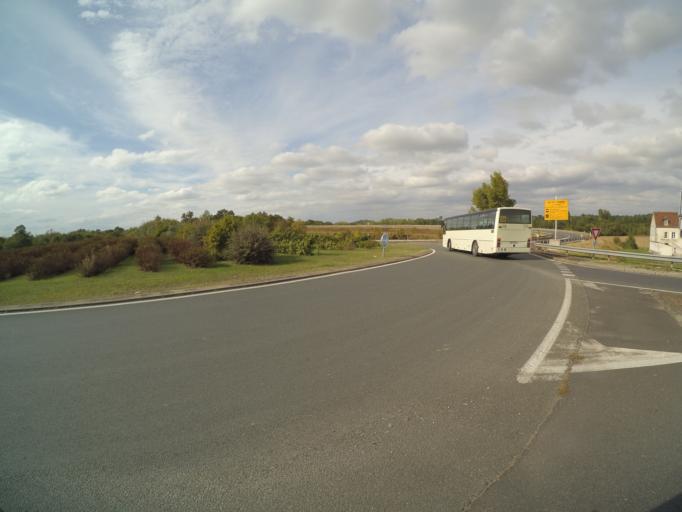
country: FR
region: Centre
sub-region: Departement d'Indre-et-Loire
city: Vouvray
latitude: 47.4040
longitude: 0.8073
